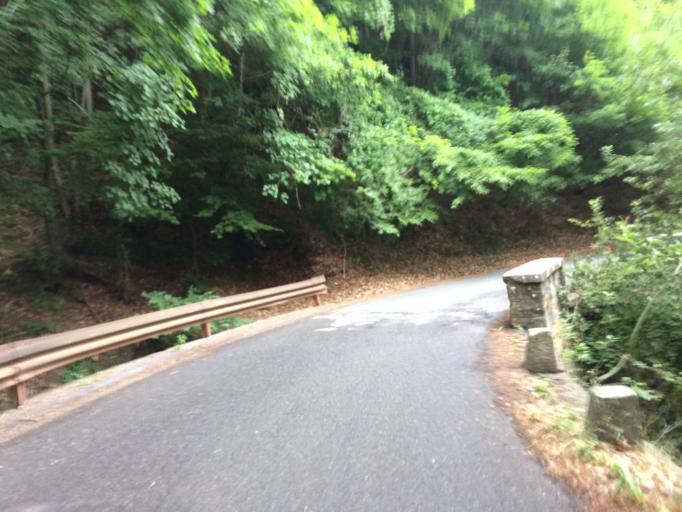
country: IT
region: Liguria
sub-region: Provincia di Imperia
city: Bajardo
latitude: 43.8773
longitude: 7.7412
